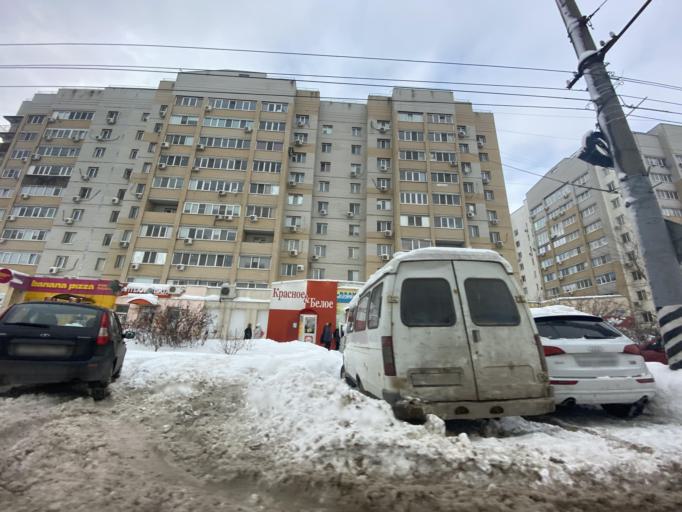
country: RU
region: Saratov
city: Engel's
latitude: 51.4981
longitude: 46.0957
